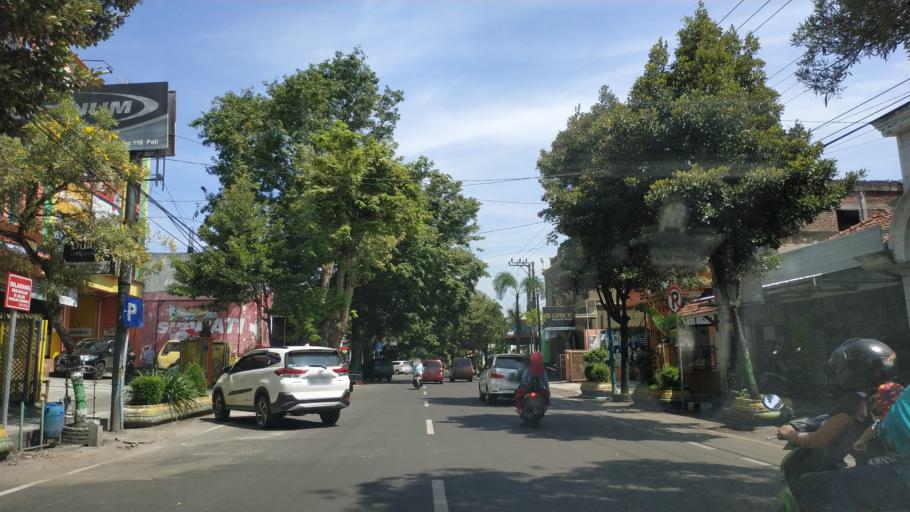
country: ID
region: Central Java
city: Pati
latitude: -6.7523
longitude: 111.0363
